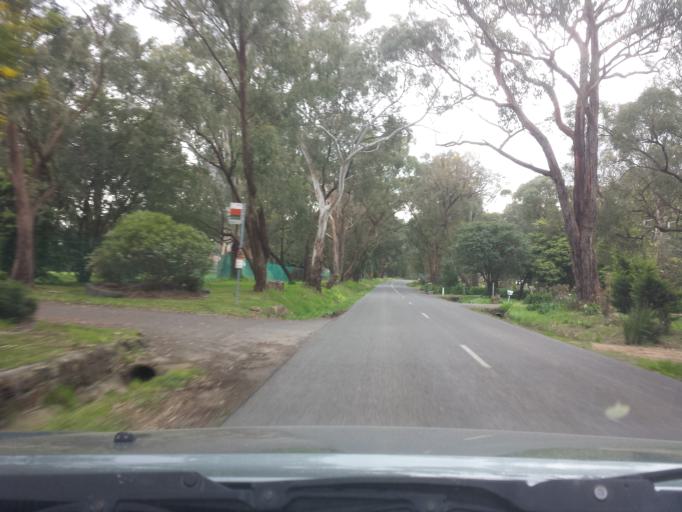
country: AU
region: Victoria
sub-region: Yarra Ranges
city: Lilydale
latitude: -37.7548
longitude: 145.3727
